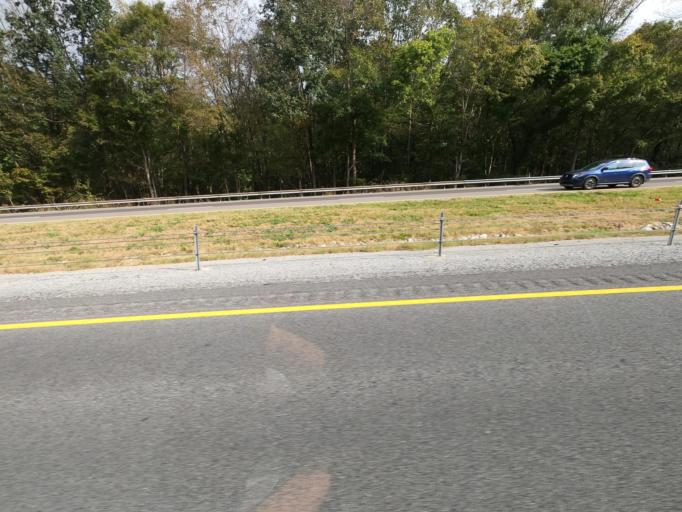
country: US
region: Tennessee
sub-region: Dickson County
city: White Bluff
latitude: 36.0273
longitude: -87.1996
